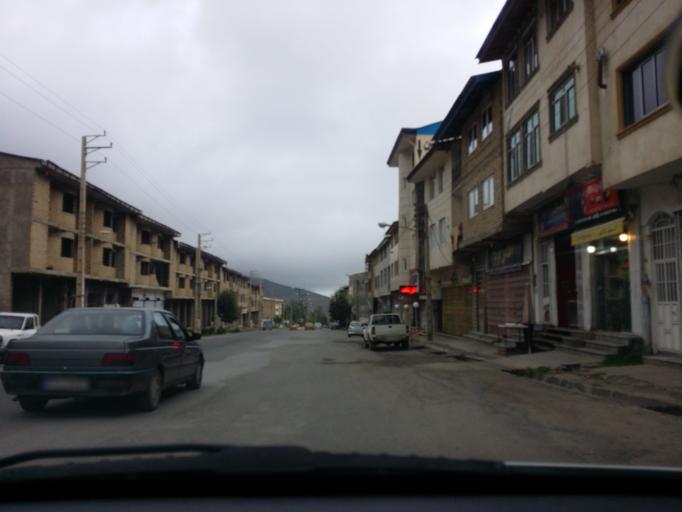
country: IR
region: Mazandaran
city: `Abbasabad
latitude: 36.4887
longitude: 51.1329
